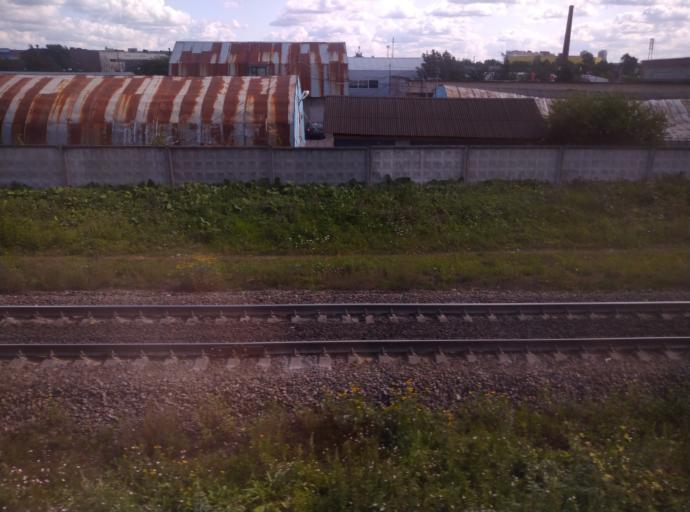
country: RU
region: St.-Petersburg
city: Centralniy
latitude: 59.9040
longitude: 30.3811
